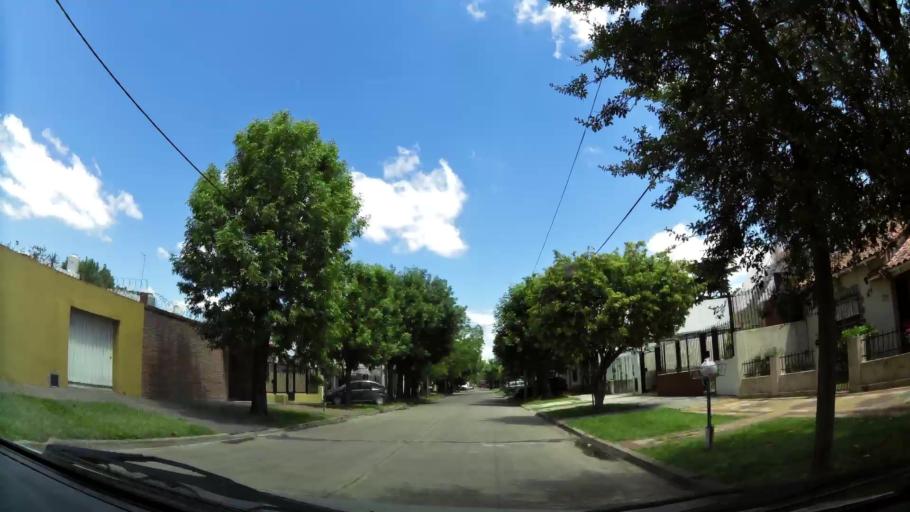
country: AR
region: Buenos Aires
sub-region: Partido de Lomas de Zamora
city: Lomas de Zamora
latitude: -34.7333
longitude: -58.4136
